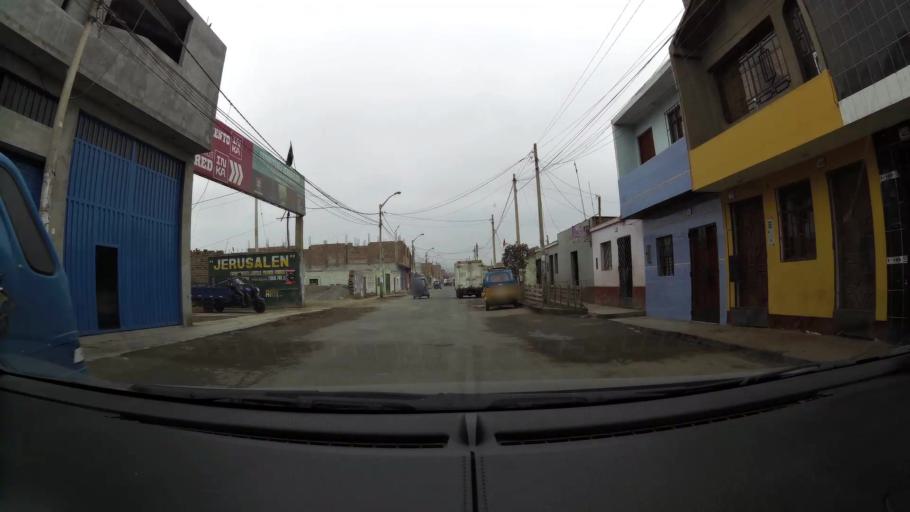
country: PE
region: Lima
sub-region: Barranca
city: Barranca
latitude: -10.7450
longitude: -77.7608
